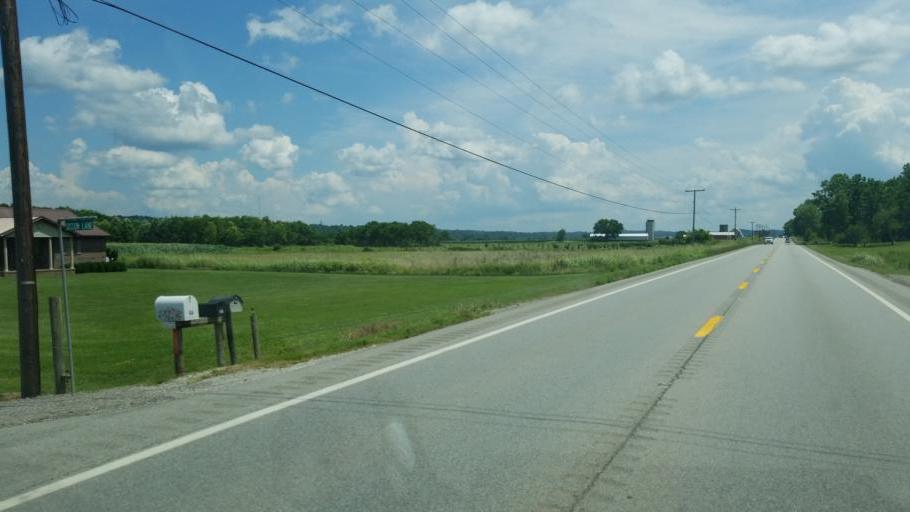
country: US
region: West Virginia
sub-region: Putnam County
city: Buffalo
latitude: 38.7616
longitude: -81.9982
